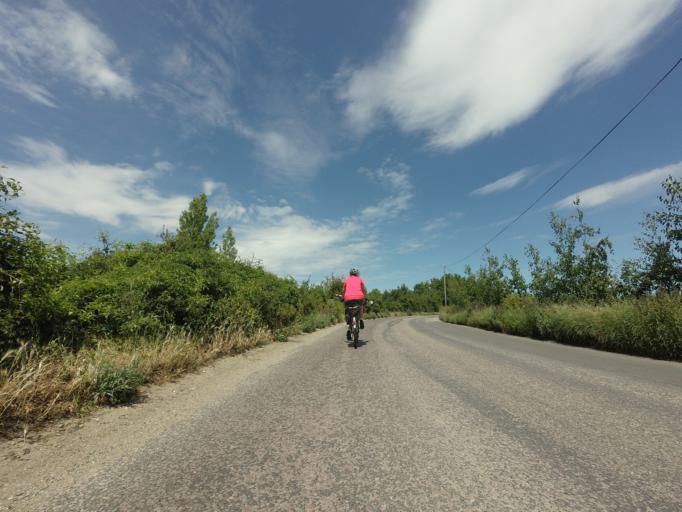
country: GB
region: England
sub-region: Kent
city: Cliffe
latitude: 51.4516
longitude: 0.4903
